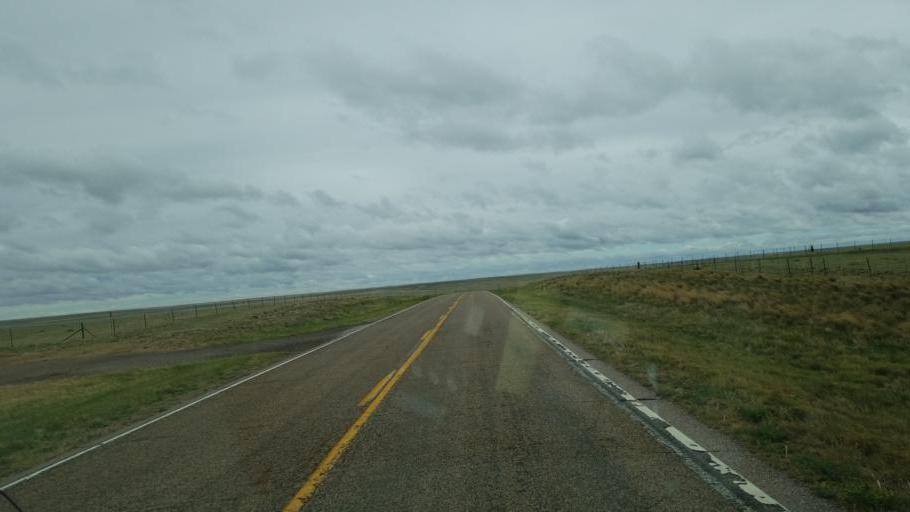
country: US
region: Colorado
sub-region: Lincoln County
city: Hugo
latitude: 38.8507
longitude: -103.4673
